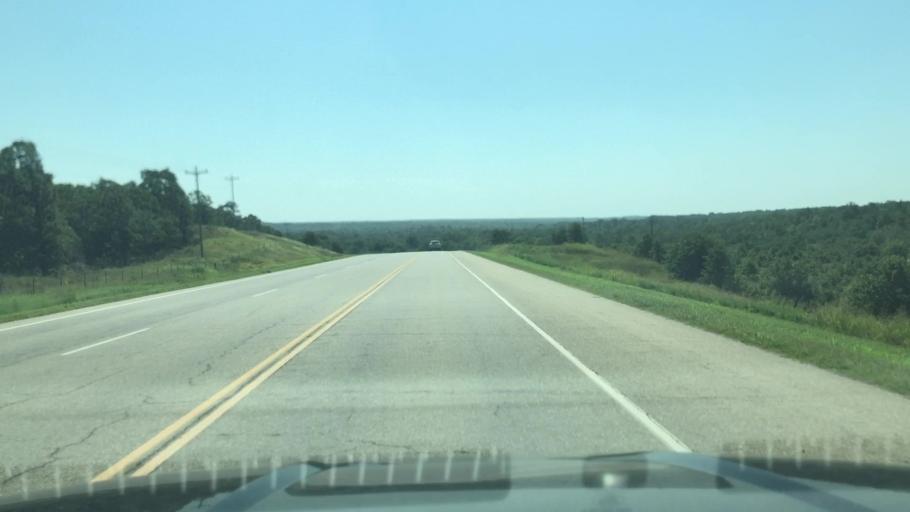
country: US
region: Oklahoma
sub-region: Creek County
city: Kellyville
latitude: 35.9877
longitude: -96.3329
